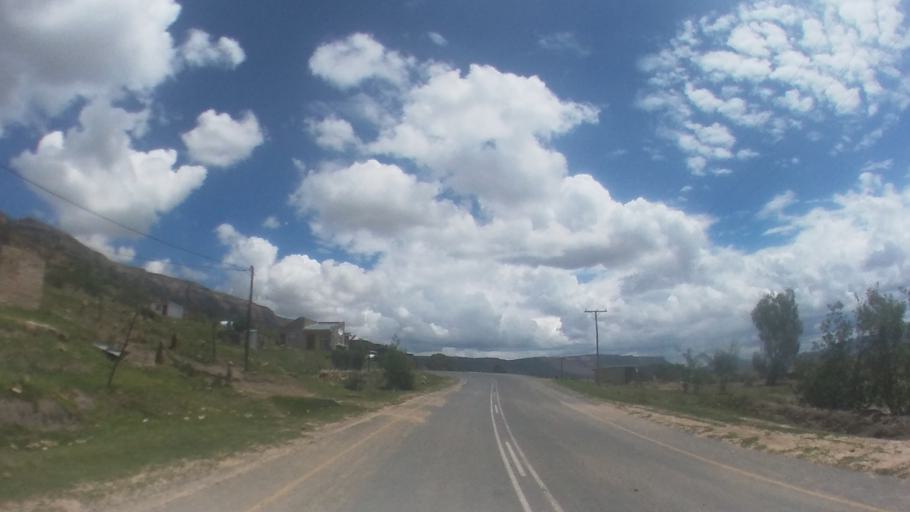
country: LS
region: Maseru
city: Maseru
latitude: -29.4688
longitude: 27.5103
